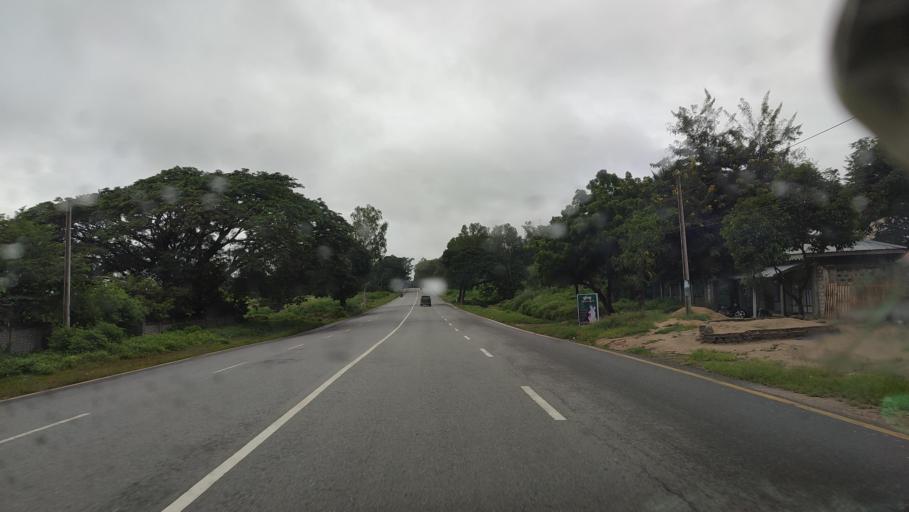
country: MM
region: Mandalay
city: Pyinmana
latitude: 19.9717
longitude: 96.2520
